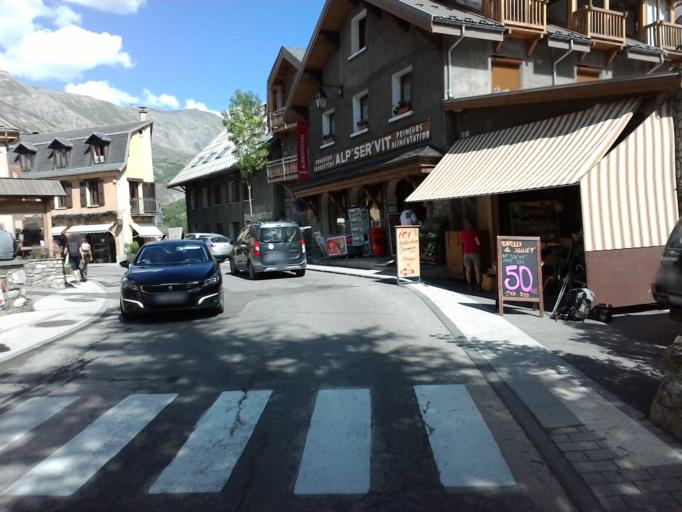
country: FR
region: Rhone-Alpes
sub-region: Departement de la Savoie
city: Valloire
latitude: 45.0450
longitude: 6.3060
